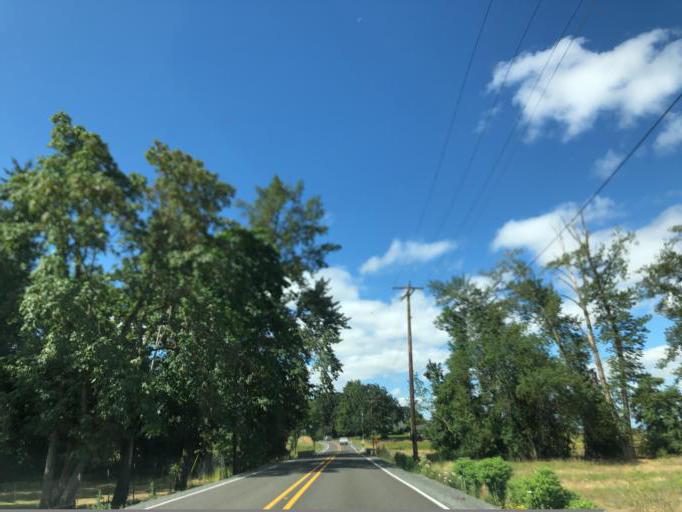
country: US
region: Oregon
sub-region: Marion County
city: Silverton
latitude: 45.0355
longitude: -122.7574
